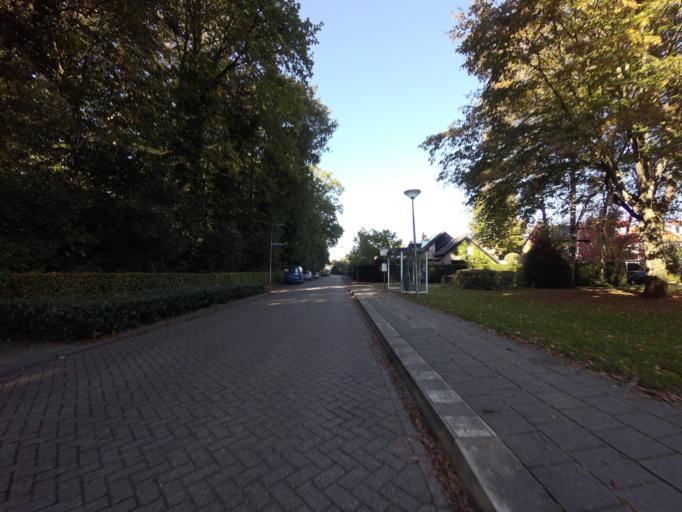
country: NL
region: North Holland
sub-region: Gemeente Naarden
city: Naarden
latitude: 52.3240
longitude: 5.1150
